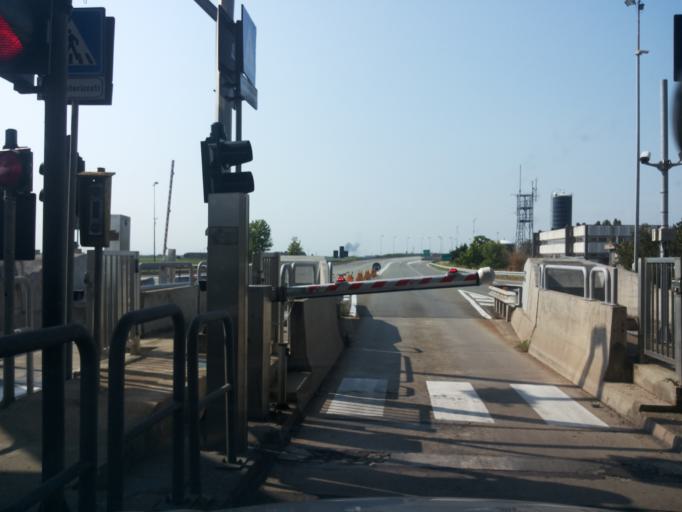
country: IT
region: Piedmont
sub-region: Provincia di Vercelli
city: Borgo Vercelli
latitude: 45.3672
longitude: 8.4889
